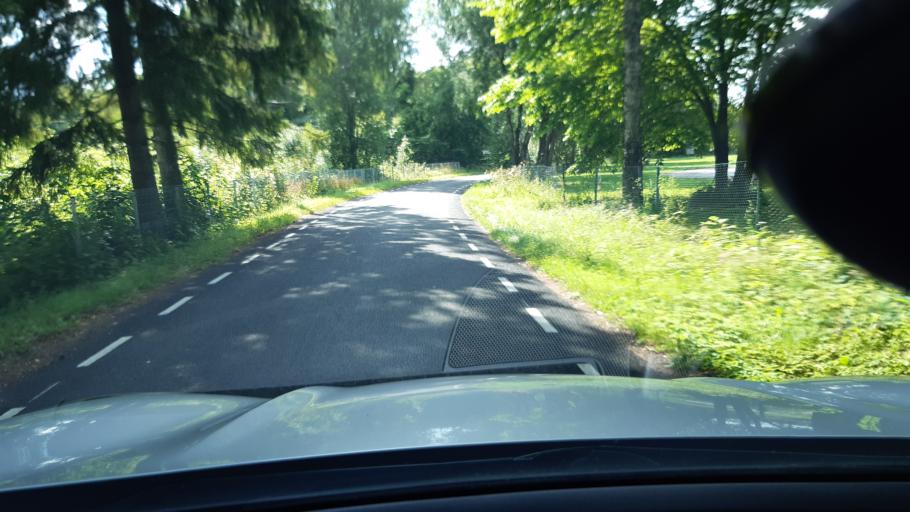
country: EE
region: Raplamaa
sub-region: Kehtna vald
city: Kehtna
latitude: 58.9395
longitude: 24.8978
